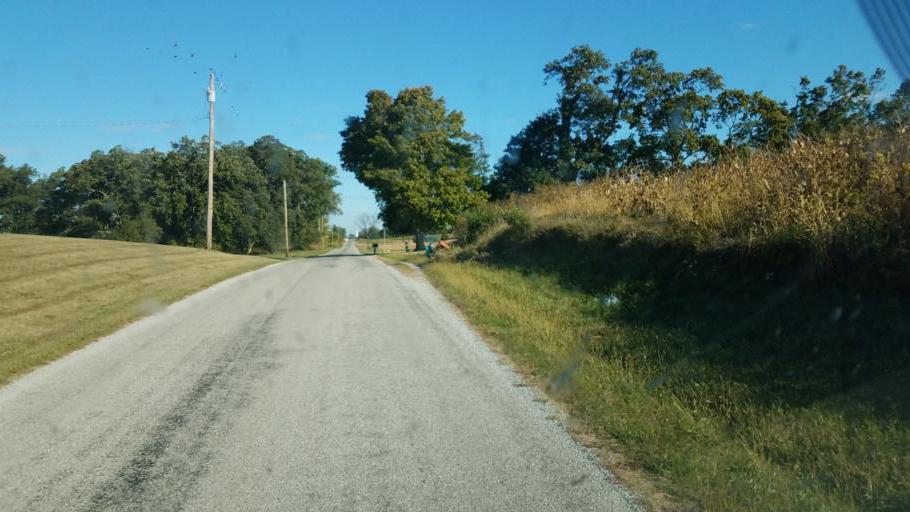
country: US
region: Ohio
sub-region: Marion County
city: Marion
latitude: 40.6923
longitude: -83.1687
